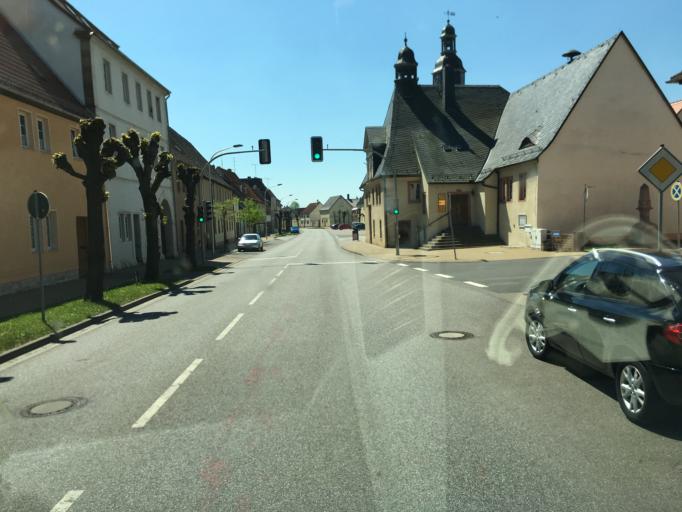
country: DE
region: Saxony-Anhalt
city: Allstedt
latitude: 51.4044
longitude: 11.3857
